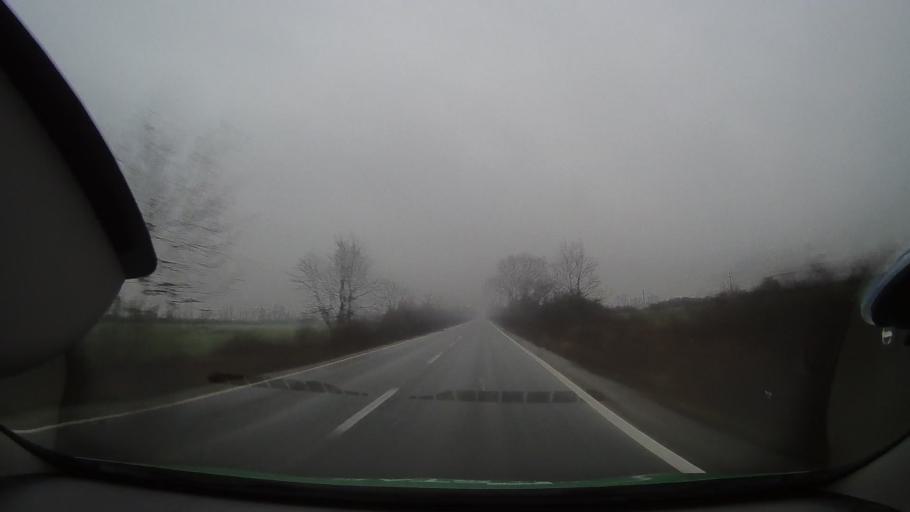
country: RO
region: Bihor
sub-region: Comuna Tinca
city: Tinca
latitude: 46.7609
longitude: 21.9348
